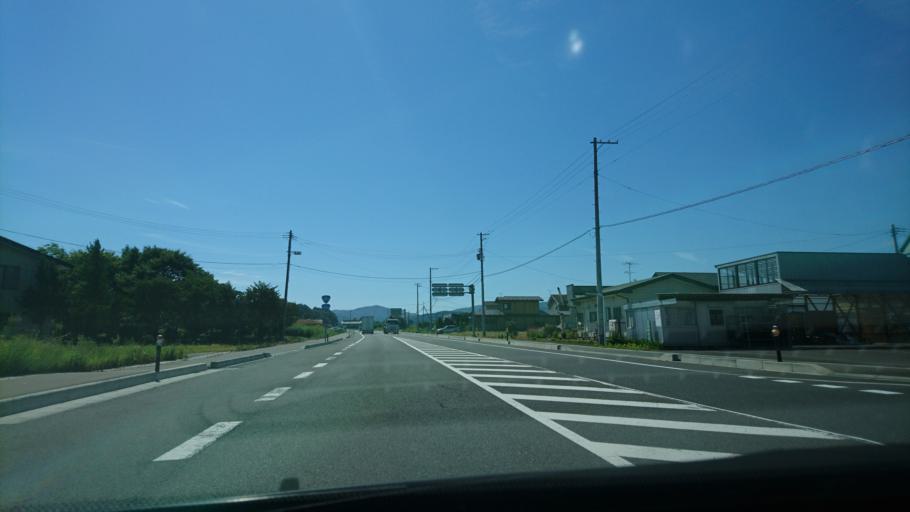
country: JP
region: Iwate
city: Tono
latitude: 39.3109
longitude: 141.5707
